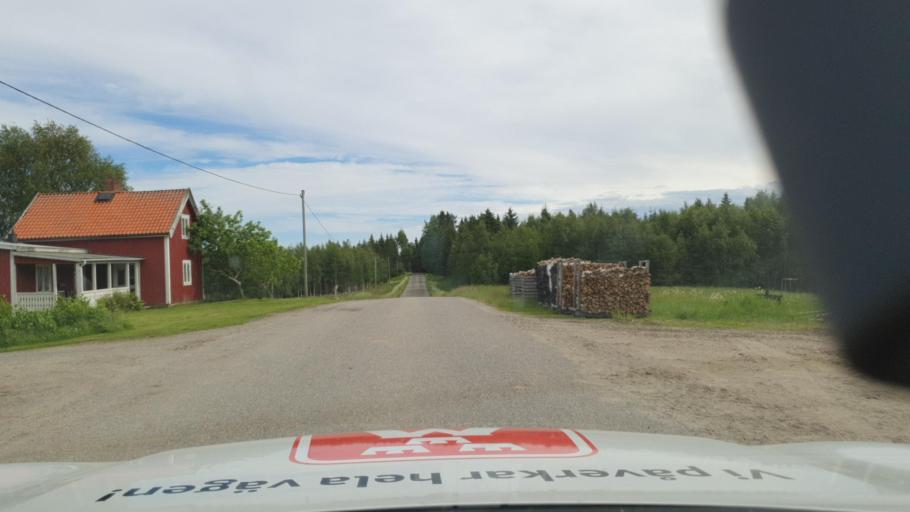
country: SE
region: Vaesterbotten
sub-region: Robertsfors Kommun
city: Robertsfors
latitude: 64.3946
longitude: 21.0194
